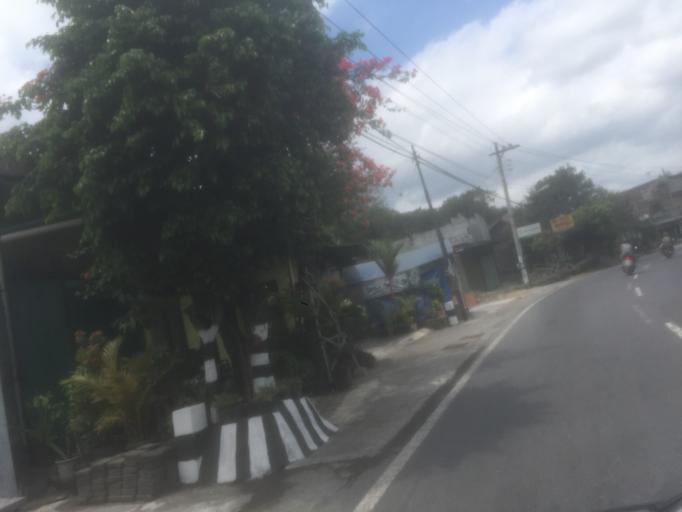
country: ID
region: Central Java
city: Muntilan
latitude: -7.6279
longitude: 110.3212
